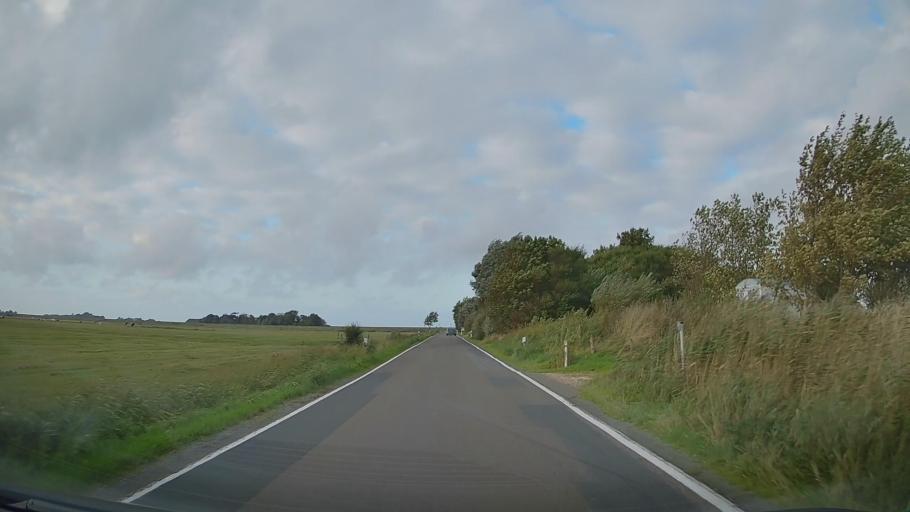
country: DE
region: Schleswig-Holstein
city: Osterhever
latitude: 54.3831
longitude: 8.7590
